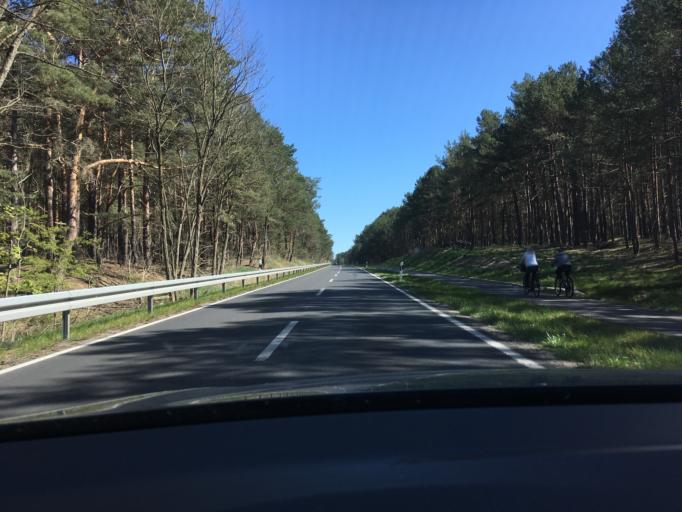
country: DE
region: Brandenburg
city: Fichtenwalde
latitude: 52.2857
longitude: 12.8621
